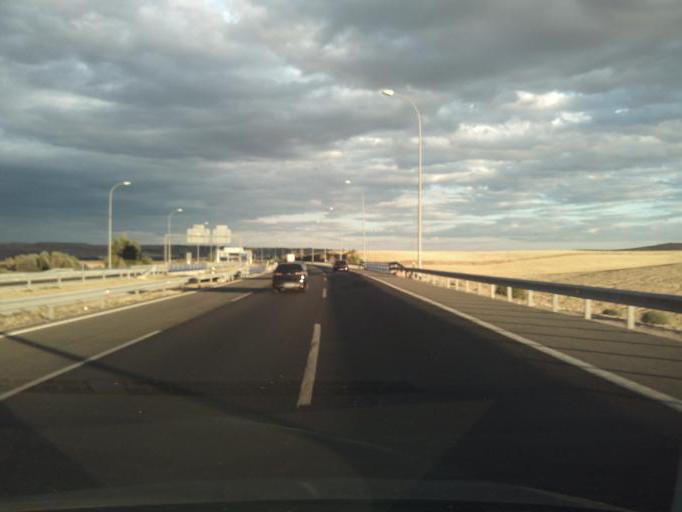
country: ES
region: Madrid
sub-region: Provincia de Madrid
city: San Sebastian de los Reyes
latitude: 40.5569
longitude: -3.5888
